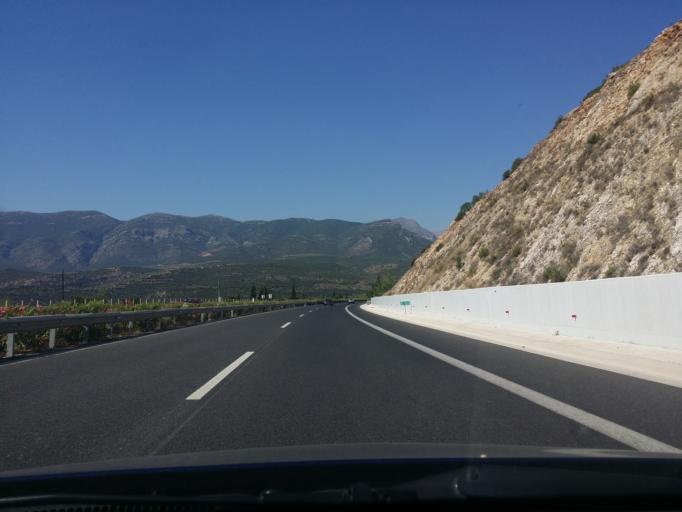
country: GR
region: Peloponnese
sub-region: Nomos Korinthias
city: Nemea
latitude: 37.7279
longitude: 22.6200
